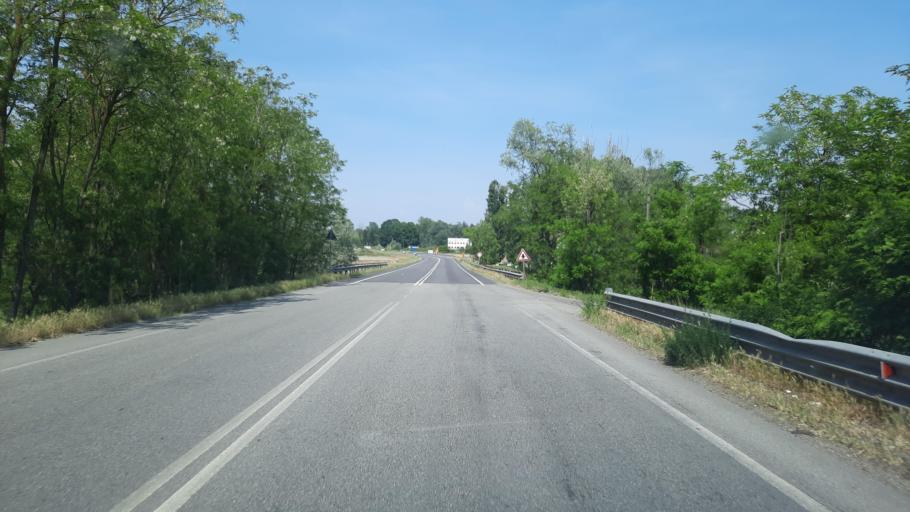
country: IT
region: Lombardy
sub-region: Provincia di Pavia
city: Mortara
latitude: 45.2451
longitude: 8.7510
